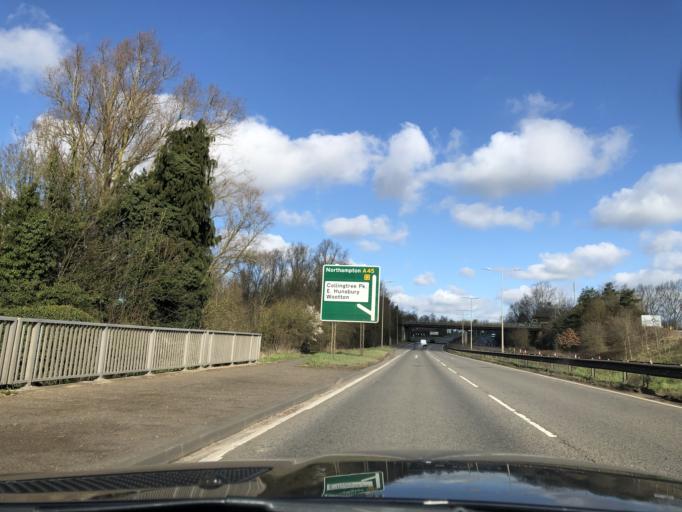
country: GB
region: England
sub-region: Northamptonshire
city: Hardingstone
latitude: 52.1969
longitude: -0.8928
